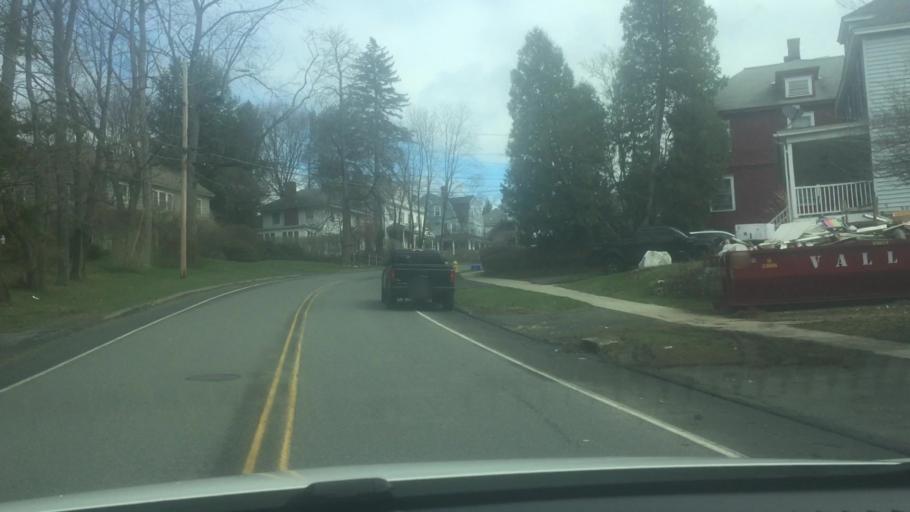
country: US
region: Massachusetts
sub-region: Berkshire County
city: Pittsfield
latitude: 42.4402
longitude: -73.2512
